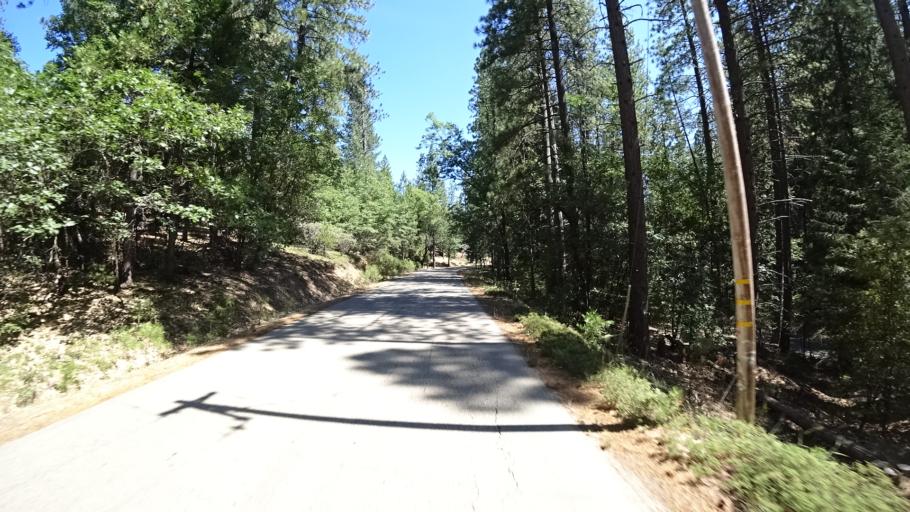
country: US
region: California
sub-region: Amador County
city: Pioneer
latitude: 38.4165
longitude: -120.4931
